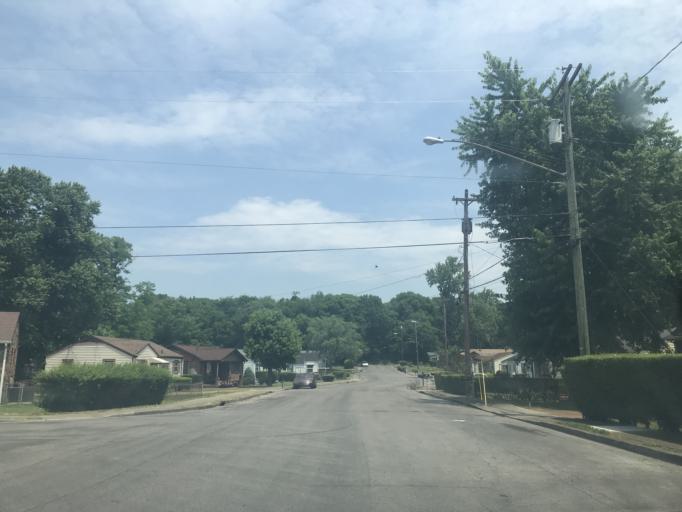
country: US
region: Tennessee
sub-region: Davidson County
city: Nashville
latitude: 36.1834
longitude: -86.8203
